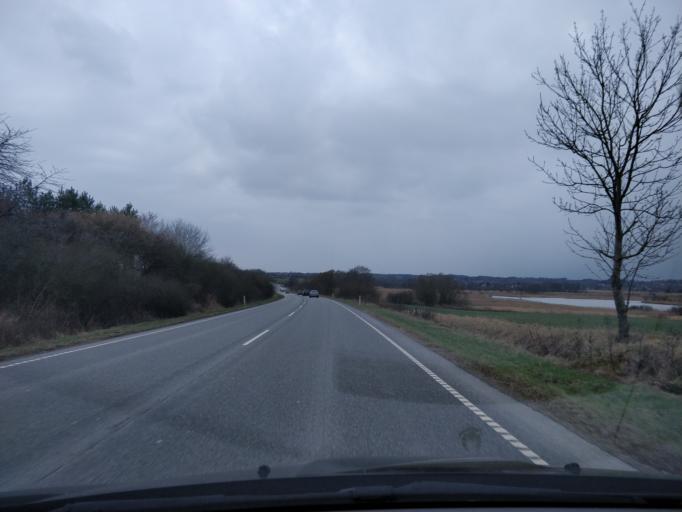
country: DK
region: South Denmark
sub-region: Fredericia Kommune
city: Fredericia
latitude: 55.6183
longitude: 9.7464
